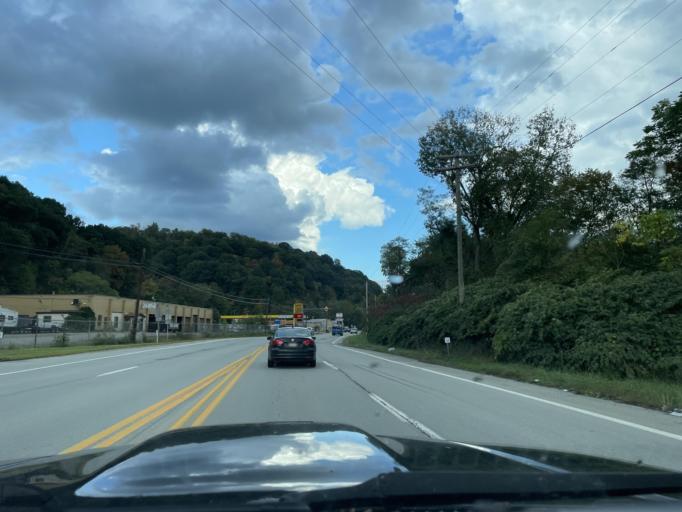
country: US
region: Pennsylvania
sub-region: Westmoreland County
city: Lower Burrell
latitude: 40.5525
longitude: -79.7550
